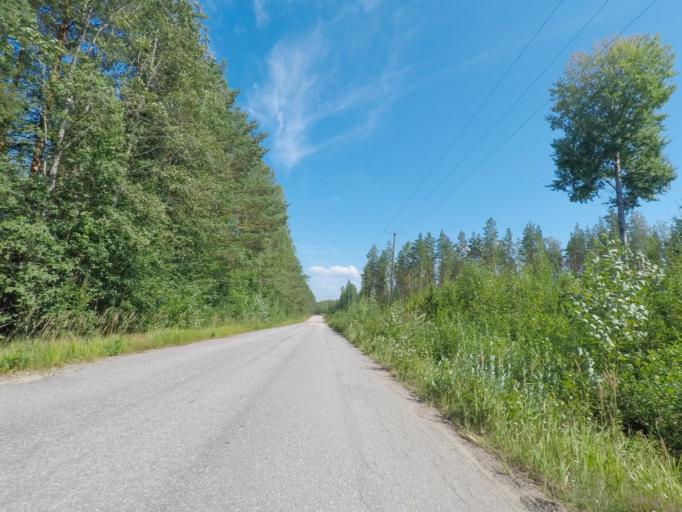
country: FI
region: Southern Savonia
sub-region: Mikkeli
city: Puumala
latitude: 61.4223
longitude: 28.1435
